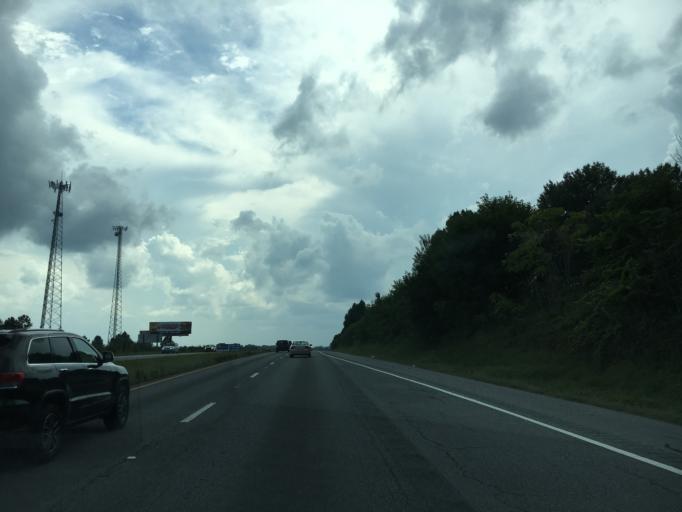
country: US
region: South Carolina
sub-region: Spartanburg County
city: Cowpens
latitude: 35.0696
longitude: -81.7645
